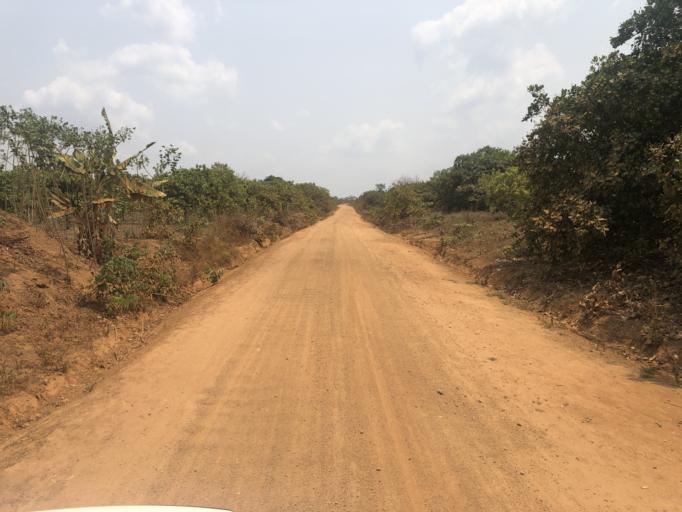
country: NG
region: Osun
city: Bode Osi
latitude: 7.8016
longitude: 4.1679
